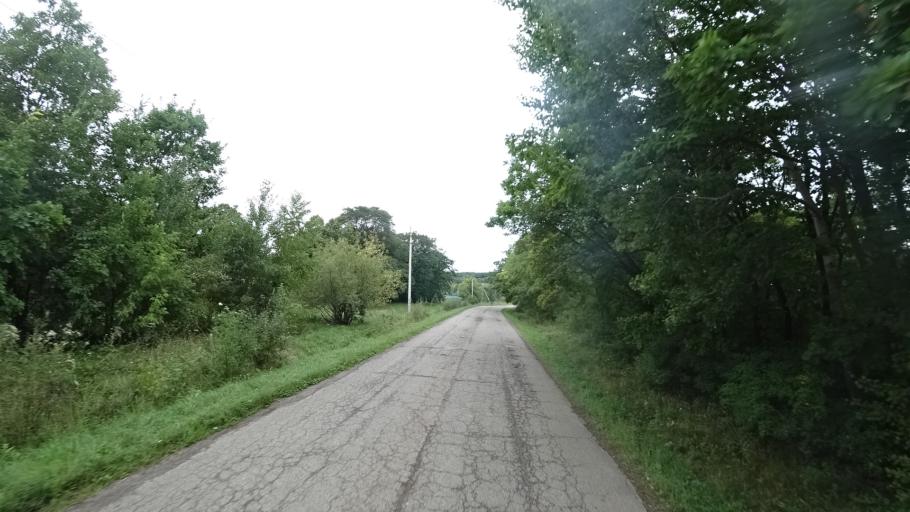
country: RU
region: Primorskiy
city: Chernigovka
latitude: 44.4554
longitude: 132.5950
